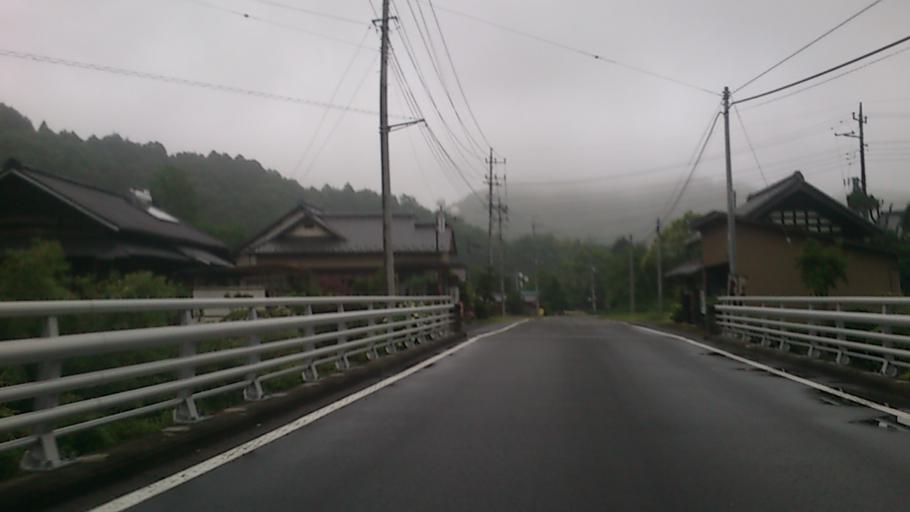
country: JP
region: Ibaraki
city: Daigo
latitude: 36.6670
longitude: 140.3160
